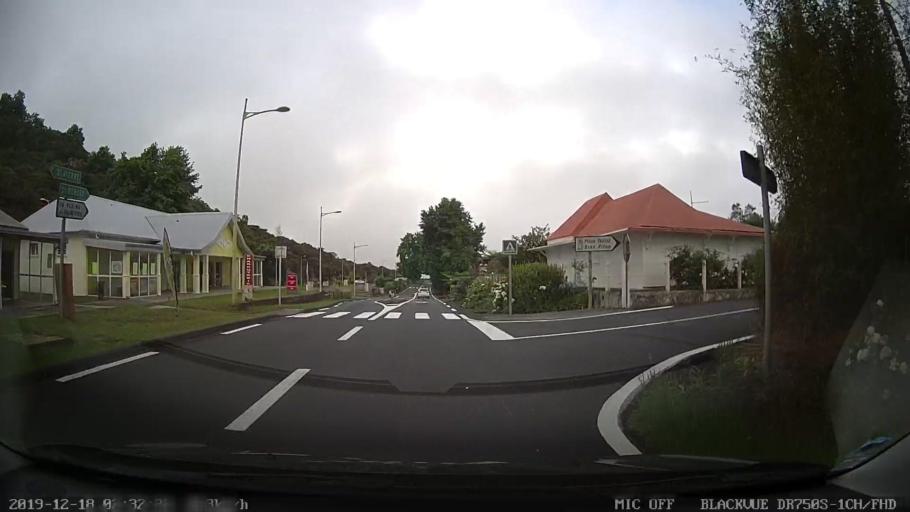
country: RE
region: Reunion
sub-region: Reunion
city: Cilaos
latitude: -21.1539
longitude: 55.6101
